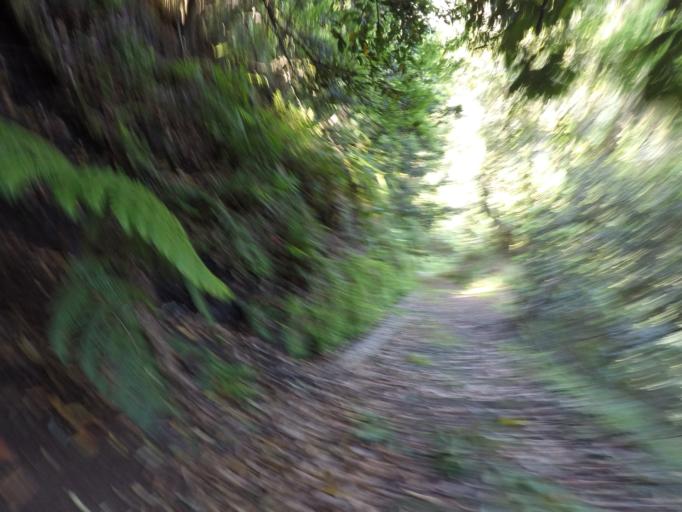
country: PT
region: Madeira
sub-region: Santana
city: Santana
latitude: 32.8223
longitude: -16.9487
